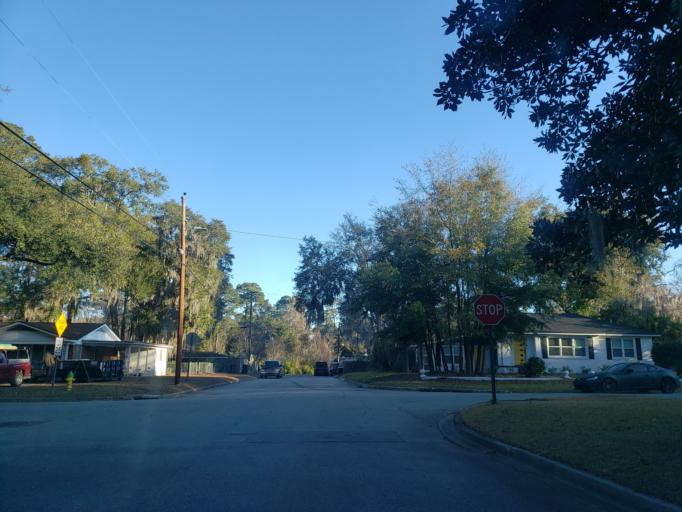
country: US
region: Georgia
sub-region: Chatham County
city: Isle of Hope
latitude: 32.0144
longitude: -81.0995
